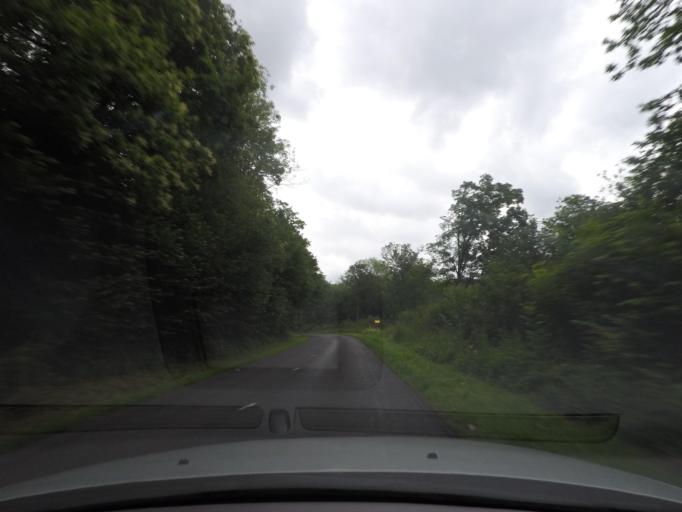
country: FR
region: Haute-Normandie
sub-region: Departement de la Seine-Maritime
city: Neufchatel-en-Bray
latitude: 49.7394
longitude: 1.4782
